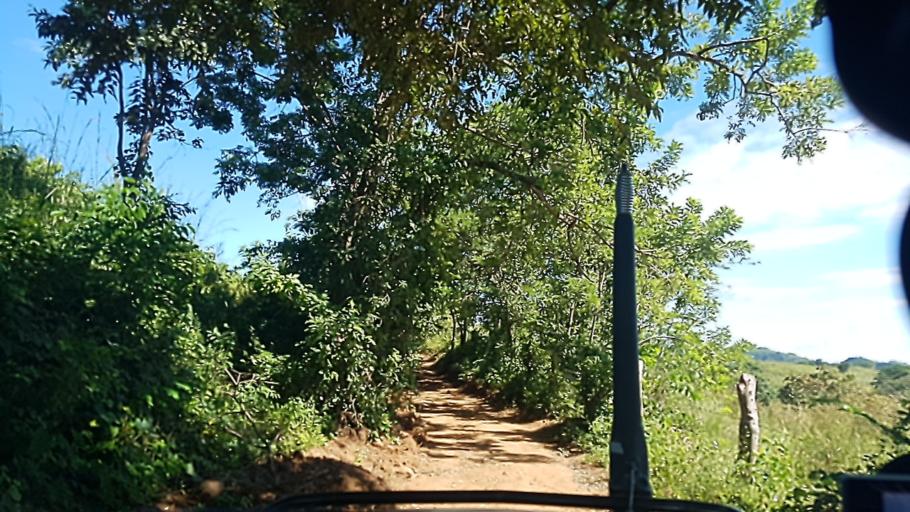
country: NI
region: Granada
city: Nandaime
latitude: 11.5779
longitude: -86.0962
